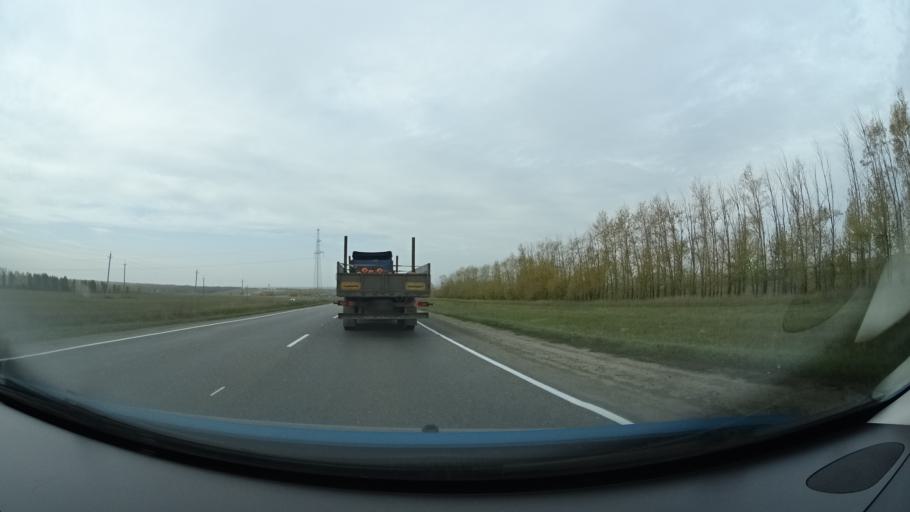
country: RU
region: Bashkortostan
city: Buzdyak
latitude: 54.6720
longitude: 54.7604
